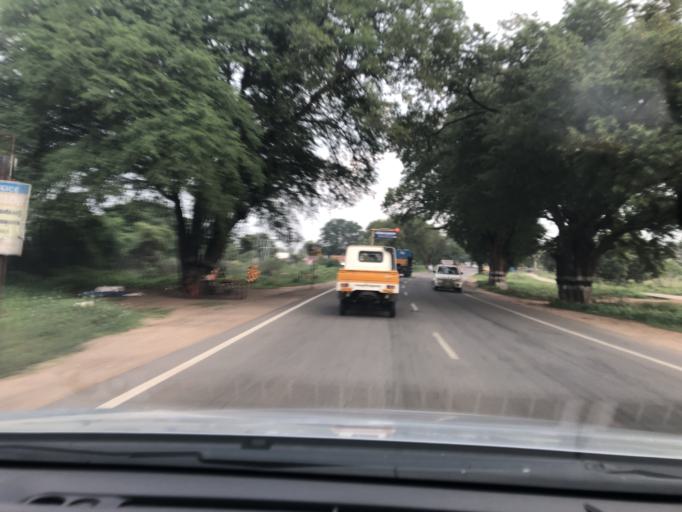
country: IN
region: Tamil Nadu
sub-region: Dindigul
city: Vedasandur
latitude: 10.4770
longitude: 77.7833
